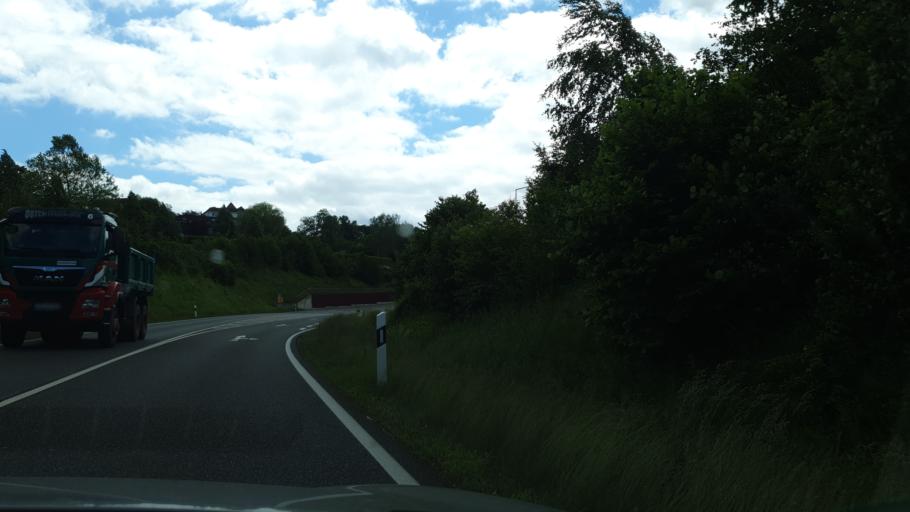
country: DE
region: Rheinland-Pfalz
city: Hohr-Grenzhausen
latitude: 50.4328
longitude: 7.6823
